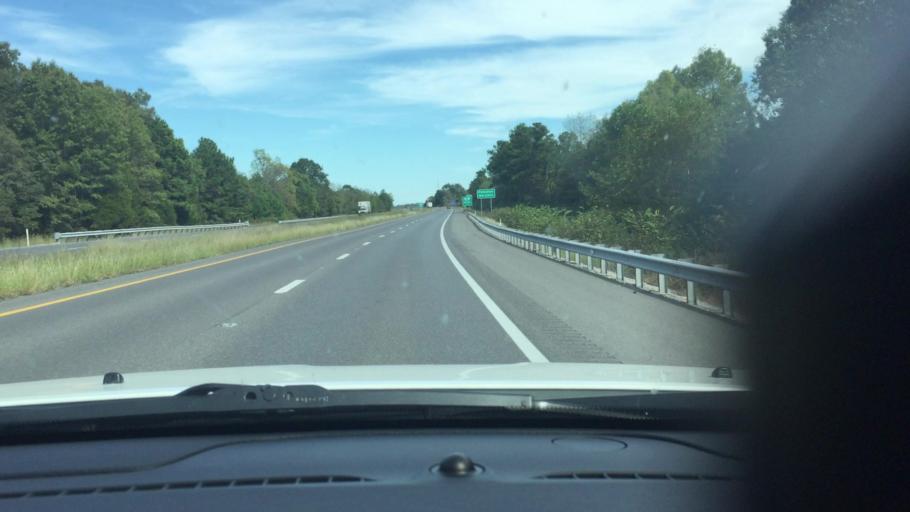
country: US
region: Kentucky
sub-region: Caldwell County
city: Princeton
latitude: 37.1176
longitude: -87.9193
